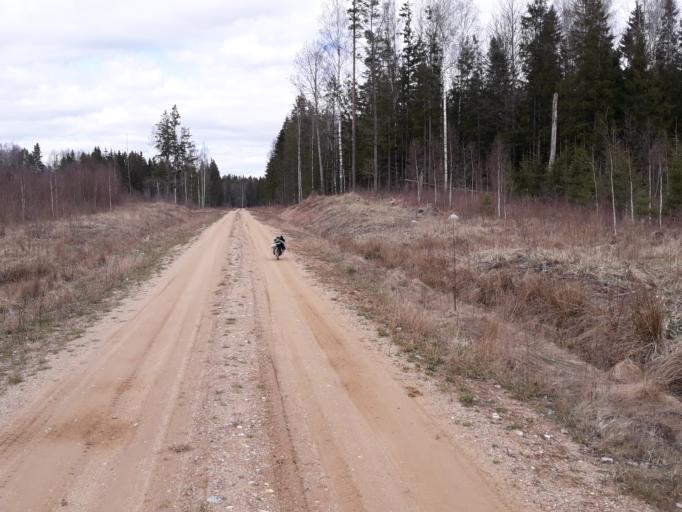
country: LV
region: Broceni
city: Broceni
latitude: 56.8869
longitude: 22.3853
